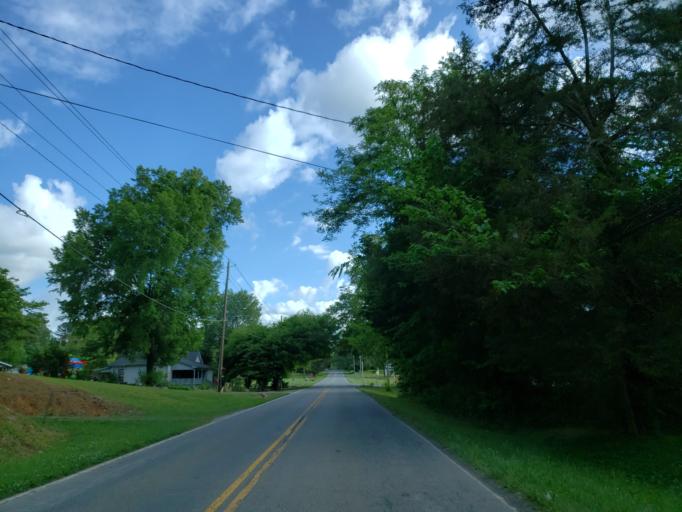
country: US
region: Georgia
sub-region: Bartow County
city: Cartersville
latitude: 34.2456
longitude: -84.8526
